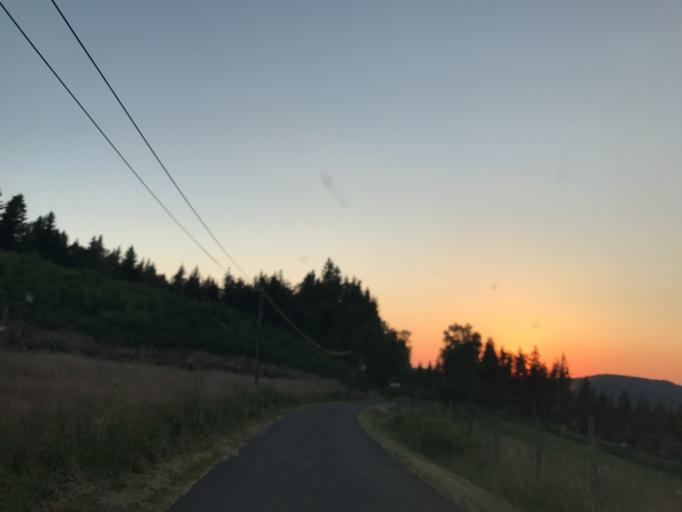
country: FR
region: Rhone-Alpes
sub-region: Departement de la Loire
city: Noiretable
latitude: 45.7767
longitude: 3.6967
